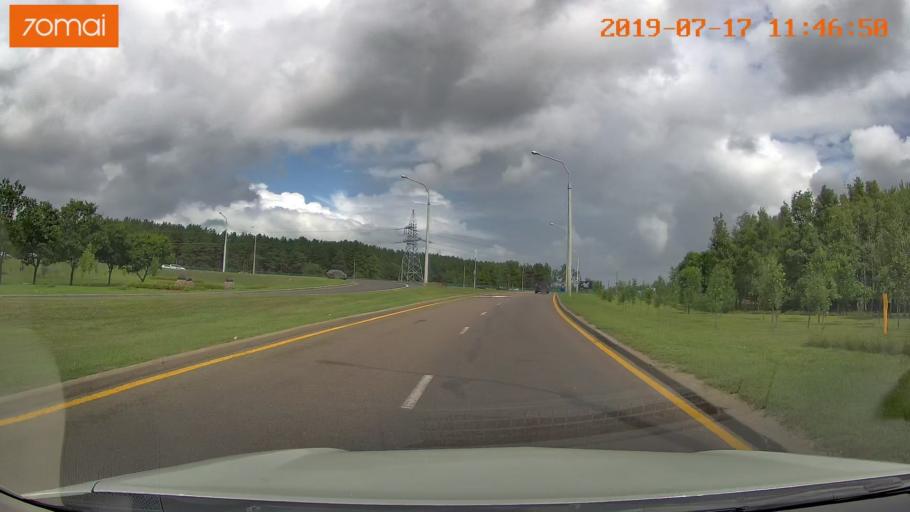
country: BY
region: Minsk
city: Zhdanovichy
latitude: 53.9505
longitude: 27.4476
